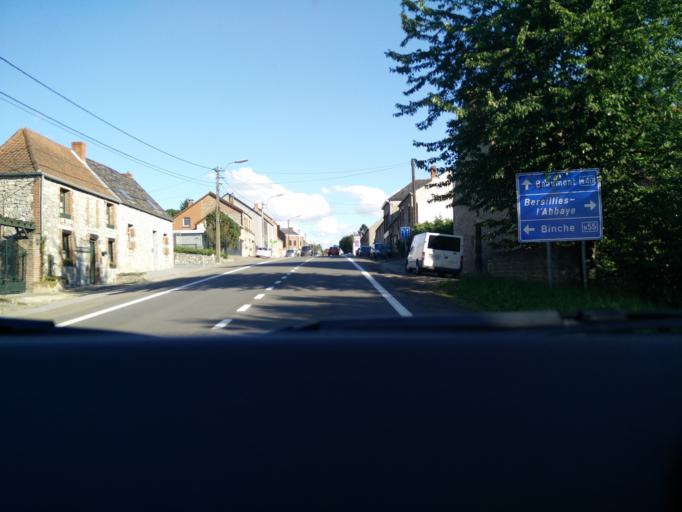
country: BE
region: Wallonia
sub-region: Province du Hainaut
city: Merbes-le-Chateau
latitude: 50.3002
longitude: 4.1563
